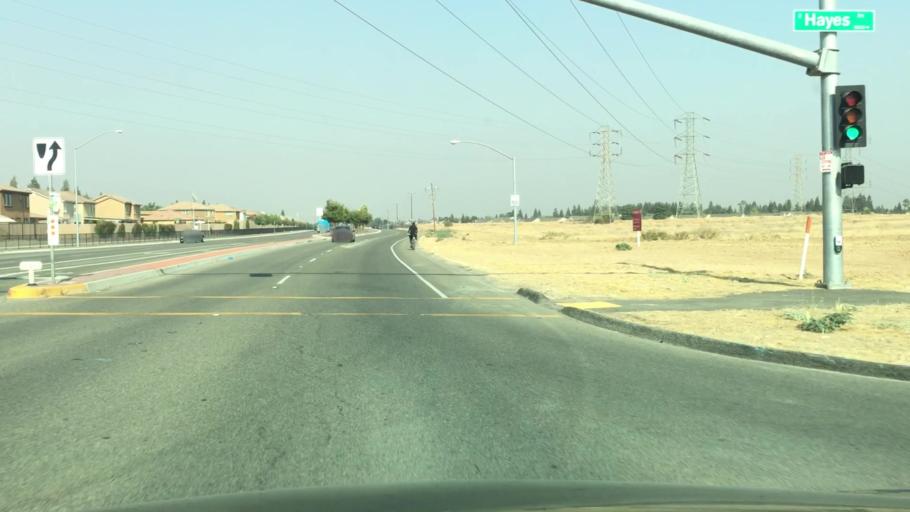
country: US
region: California
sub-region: Fresno County
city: Biola
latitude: 36.8368
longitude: -119.9014
